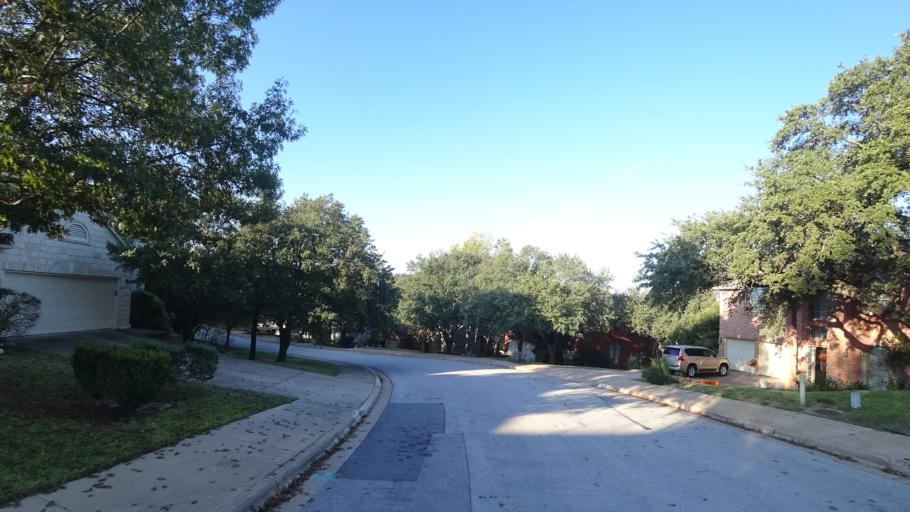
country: US
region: Texas
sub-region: Travis County
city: Hudson Bend
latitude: 30.3757
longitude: -97.8878
